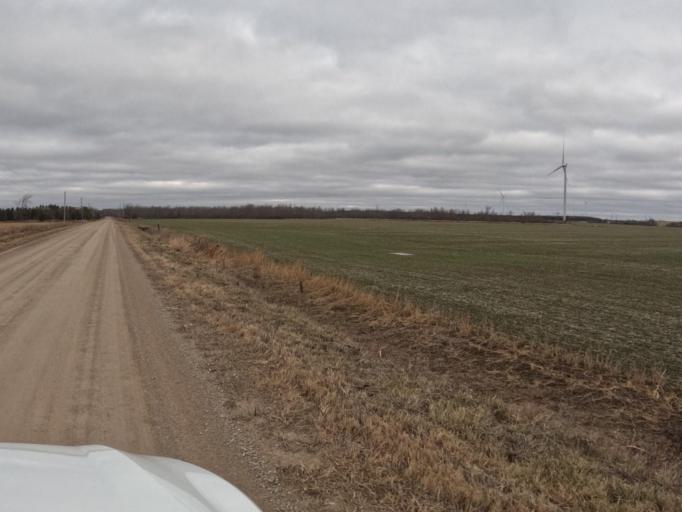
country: CA
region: Ontario
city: Shelburne
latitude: 43.8889
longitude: -80.3828
